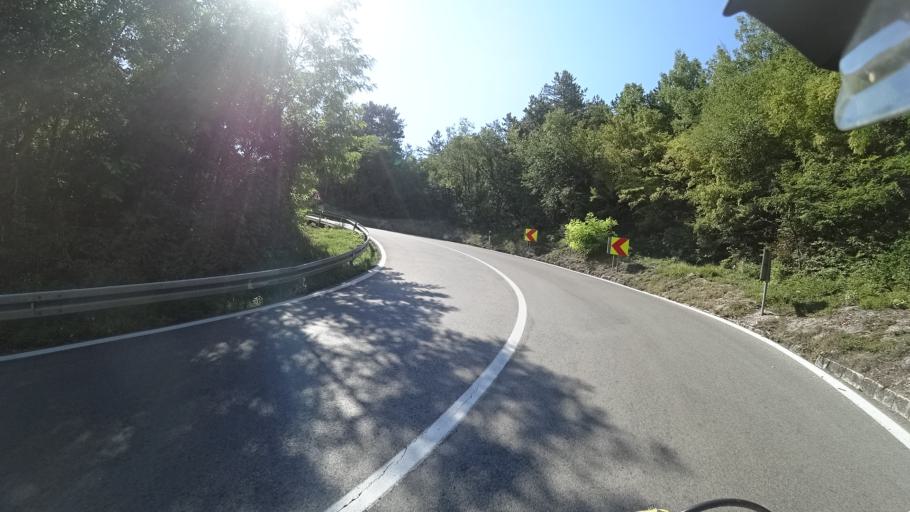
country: HR
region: Sibensko-Kniniska
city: Knin
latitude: 44.0165
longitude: 16.1959
